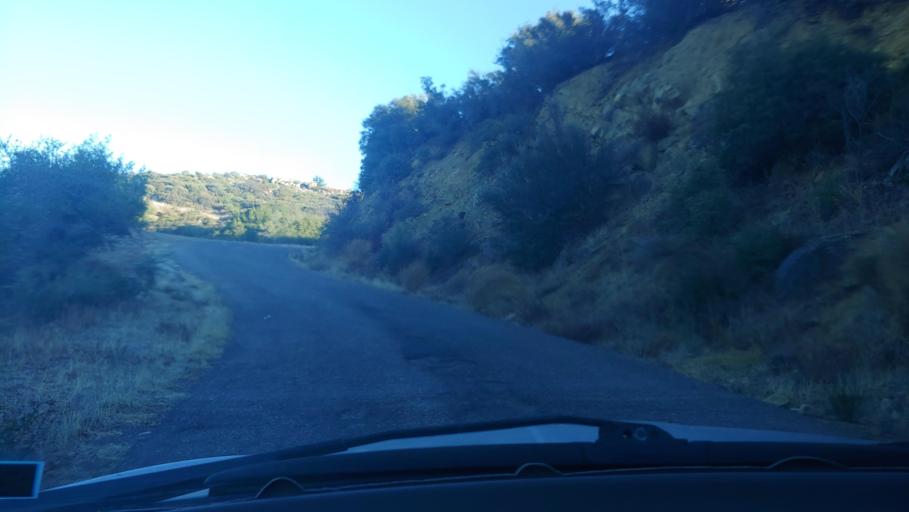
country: US
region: California
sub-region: Santa Barbara County
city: Mission Canyon
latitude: 34.5113
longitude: -119.7739
